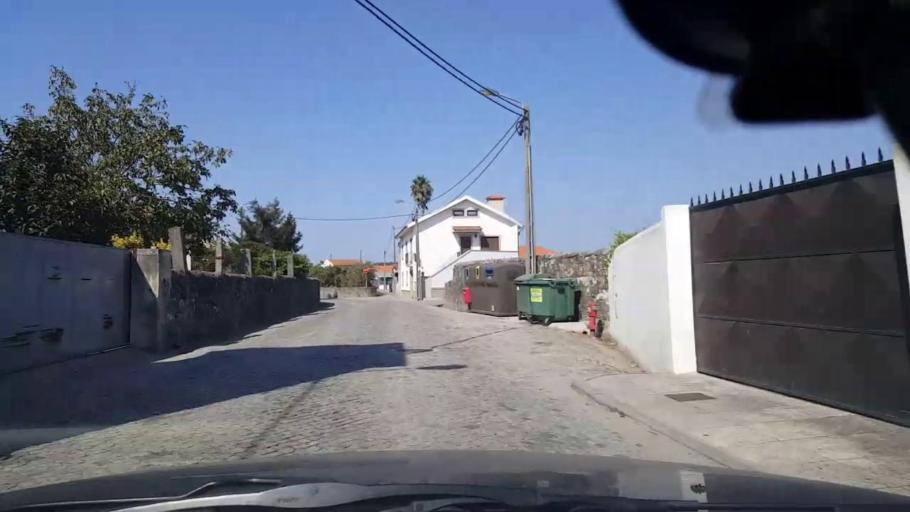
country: PT
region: Porto
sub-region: Vila do Conde
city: Arvore
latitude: 41.3860
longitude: -8.7055
